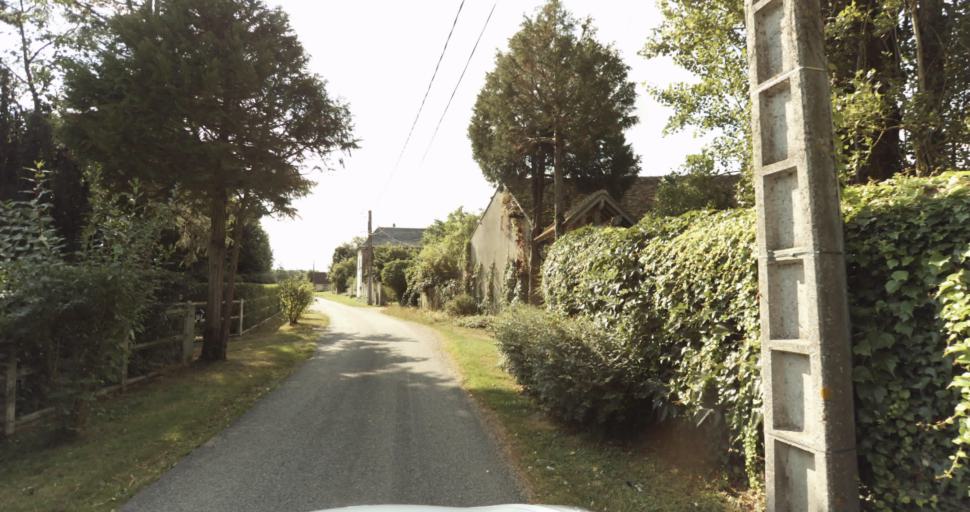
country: FR
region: Haute-Normandie
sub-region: Departement de l'Eure
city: Tillieres-sur-Avre
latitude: 48.7469
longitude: 1.1178
